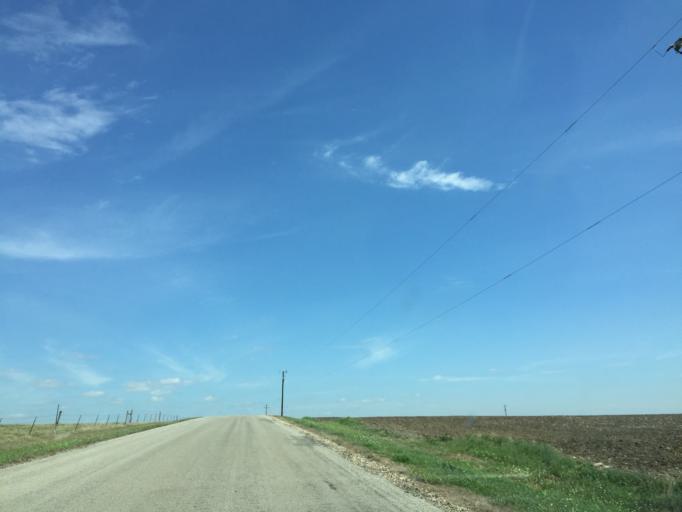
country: US
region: Texas
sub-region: Williamson County
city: Taylor
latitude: 30.5525
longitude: -97.3255
